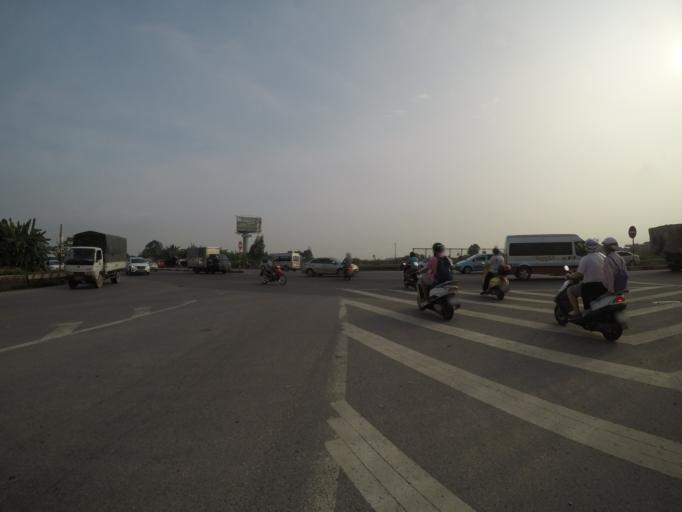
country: VN
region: Ha Noi
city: Me Linh
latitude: 21.2194
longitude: 105.7738
